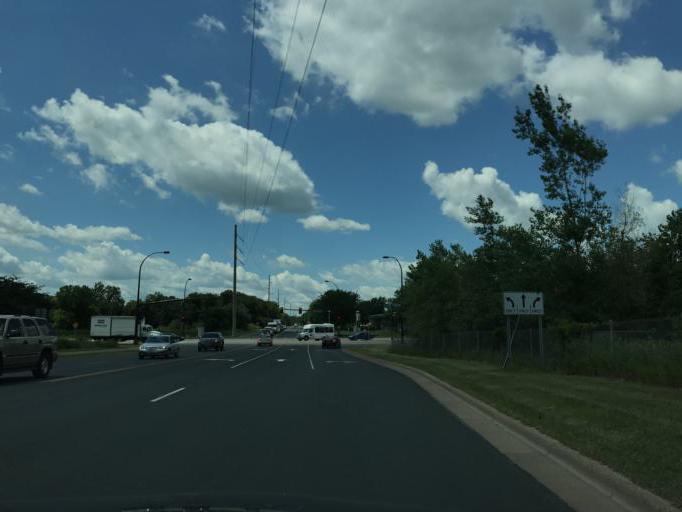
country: US
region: Minnesota
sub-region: Hennepin County
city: Maple Grove
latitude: 45.0874
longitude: -93.4298
